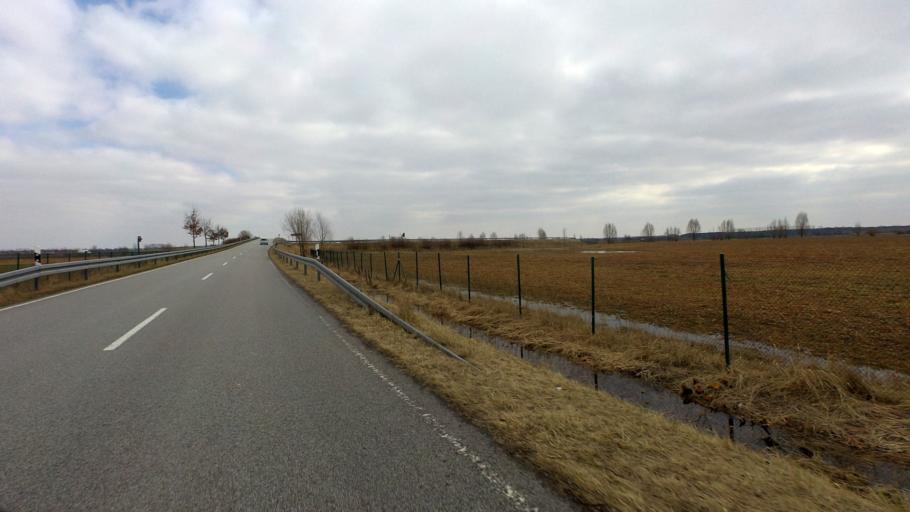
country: DE
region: Brandenburg
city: Trebbin
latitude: 52.1857
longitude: 13.2469
